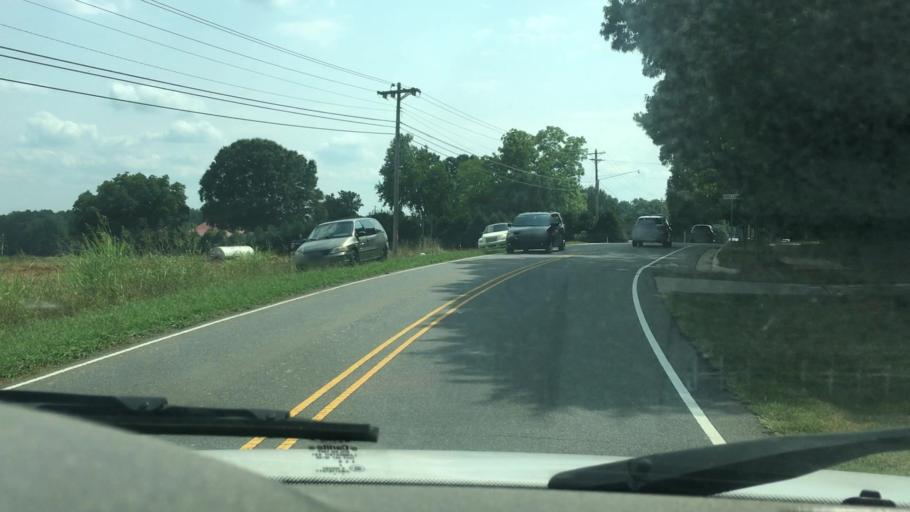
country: US
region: North Carolina
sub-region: Mecklenburg County
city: Huntersville
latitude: 35.4192
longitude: -80.8657
